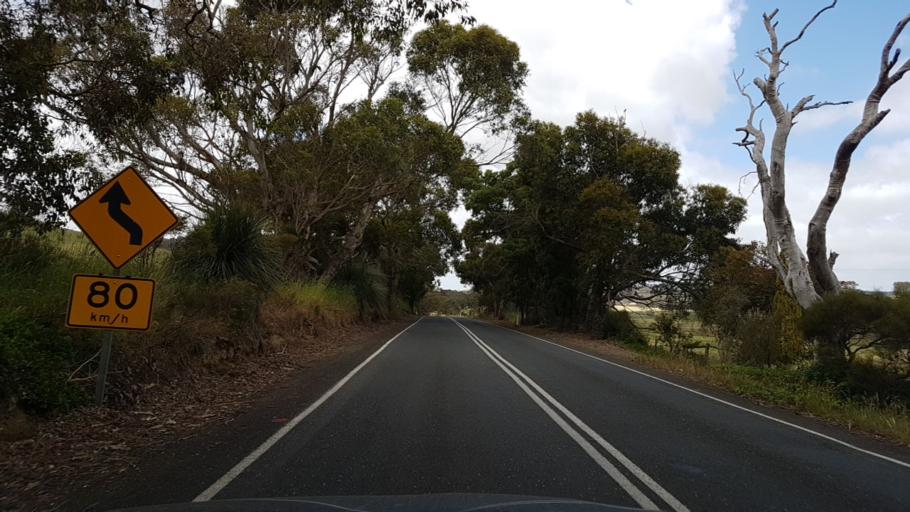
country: AU
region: South Australia
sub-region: Alexandrina
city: Mount Compass
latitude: -35.4075
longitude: 138.5345
